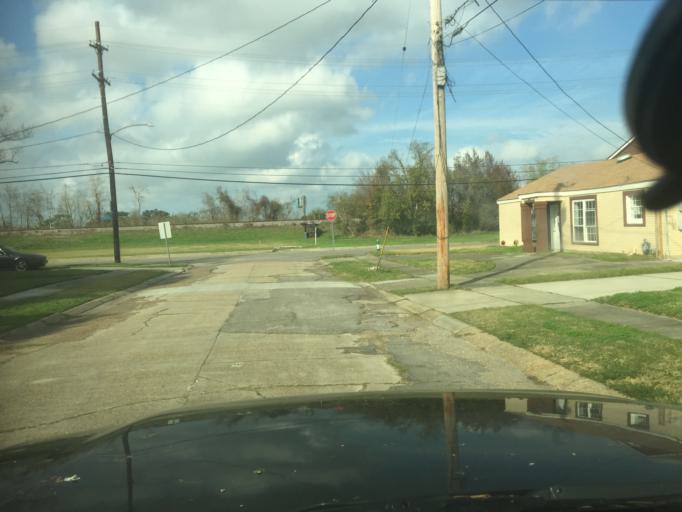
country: US
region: Louisiana
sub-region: Orleans Parish
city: New Orleans
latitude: 29.9915
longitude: -90.0803
